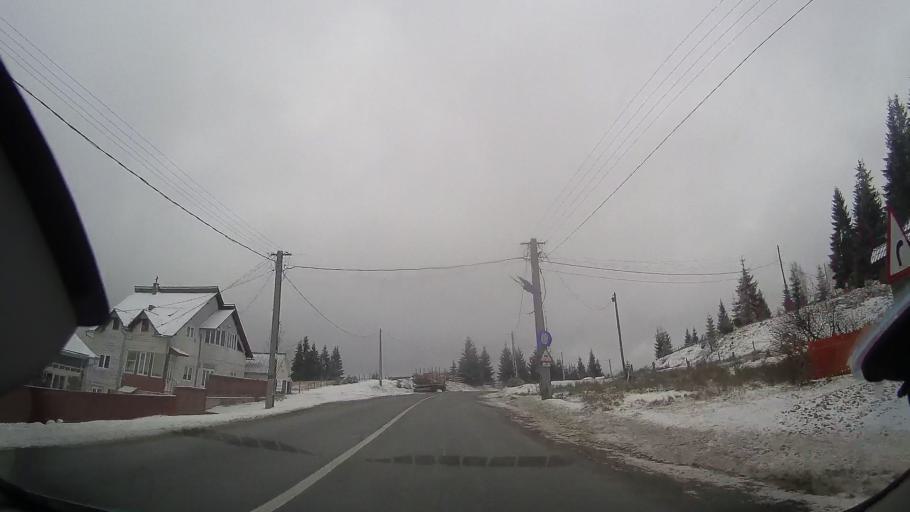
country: RO
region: Cluj
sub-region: Comuna Belis
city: Belis
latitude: 46.6854
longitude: 23.0335
